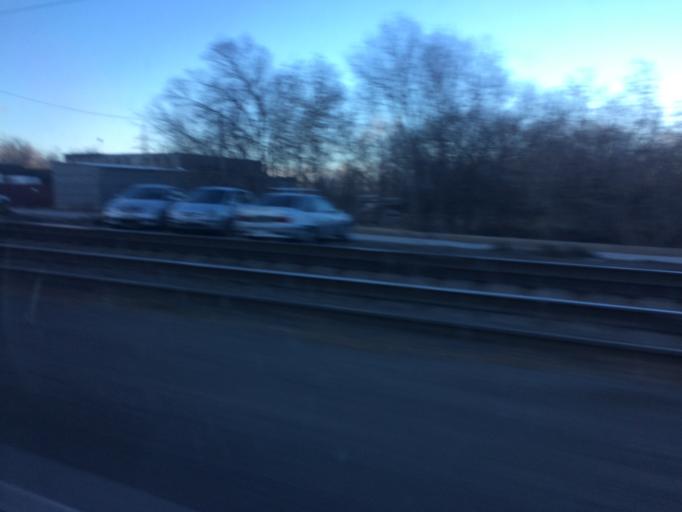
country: RU
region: Chelyabinsk
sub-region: Gorod Magnitogorsk
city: Magnitogorsk
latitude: 53.4006
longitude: 59.0251
